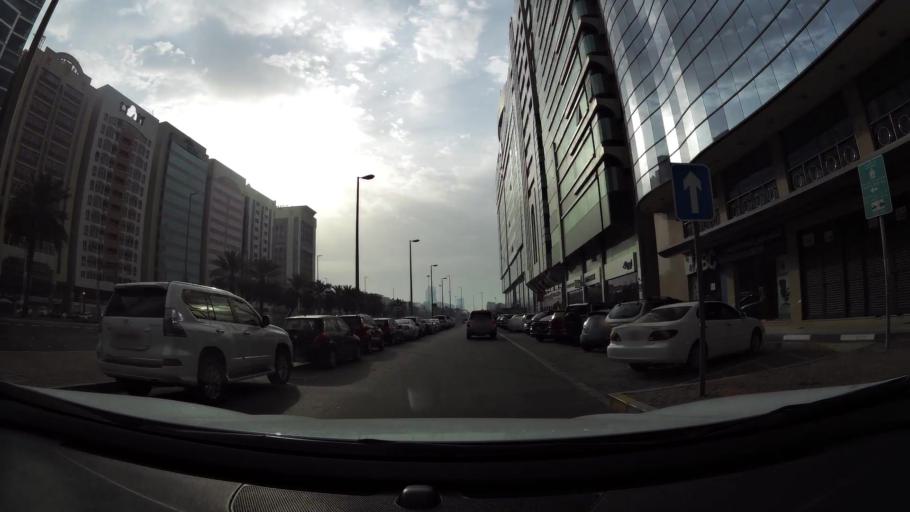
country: AE
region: Abu Dhabi
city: Abu Dhabi
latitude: 24.4750
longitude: 54.3734
